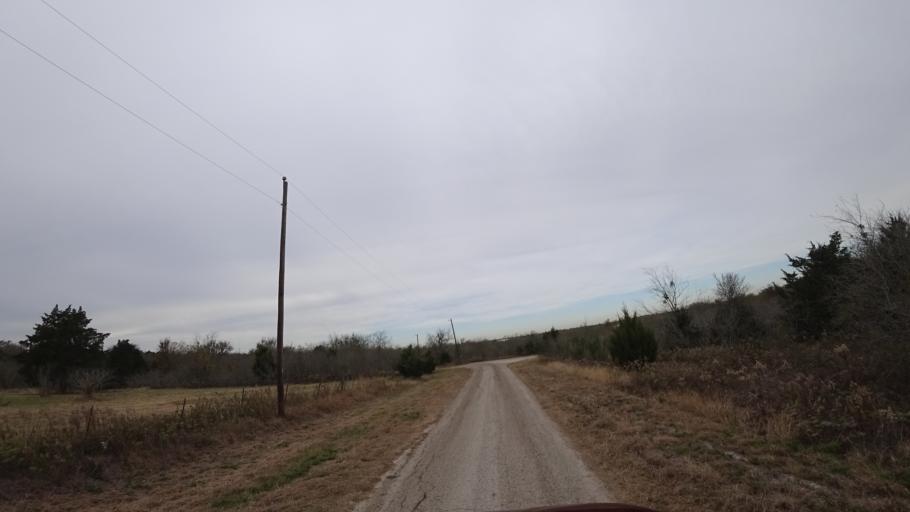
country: US
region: Texas
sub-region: Travis County
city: Garfield
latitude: 30.1107
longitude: -97.5880
